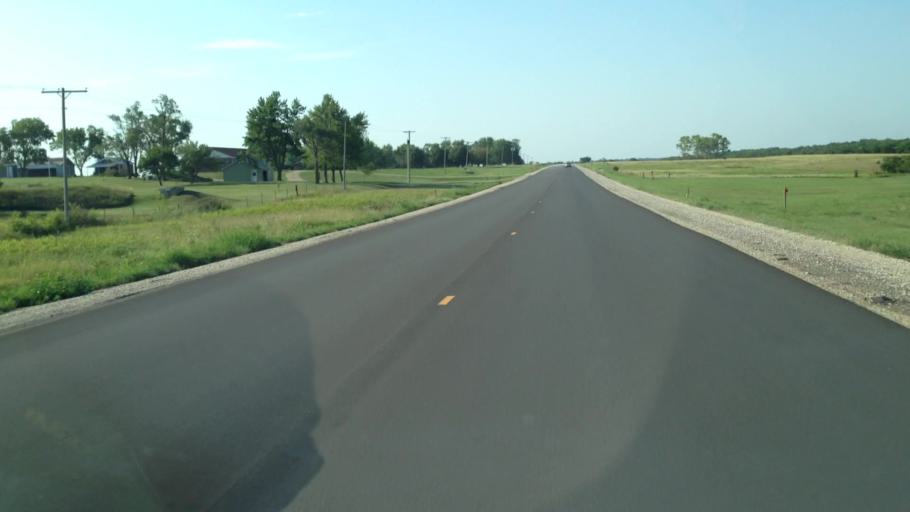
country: US
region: Kansas
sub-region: Anderson County
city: Garnett
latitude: 38.3008
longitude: -95.2489
